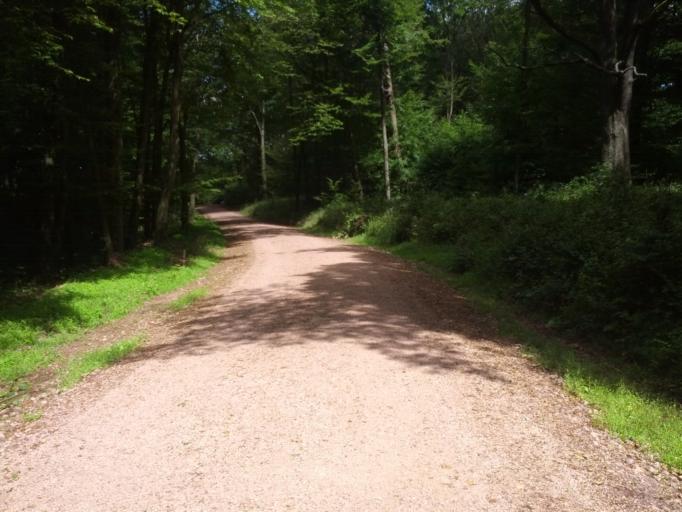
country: DE
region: Thuringia
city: Eisenach
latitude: 50.9400
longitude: 10.3252
